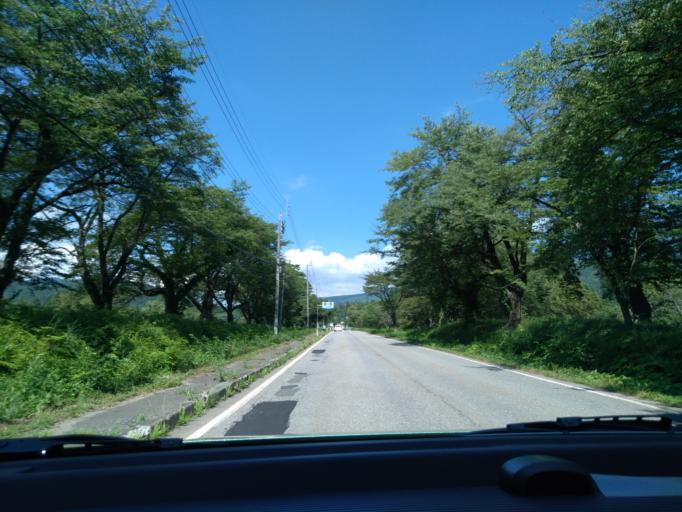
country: JP
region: Akita
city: Kakunodatemachi
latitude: 39.7543
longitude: 140.7293
